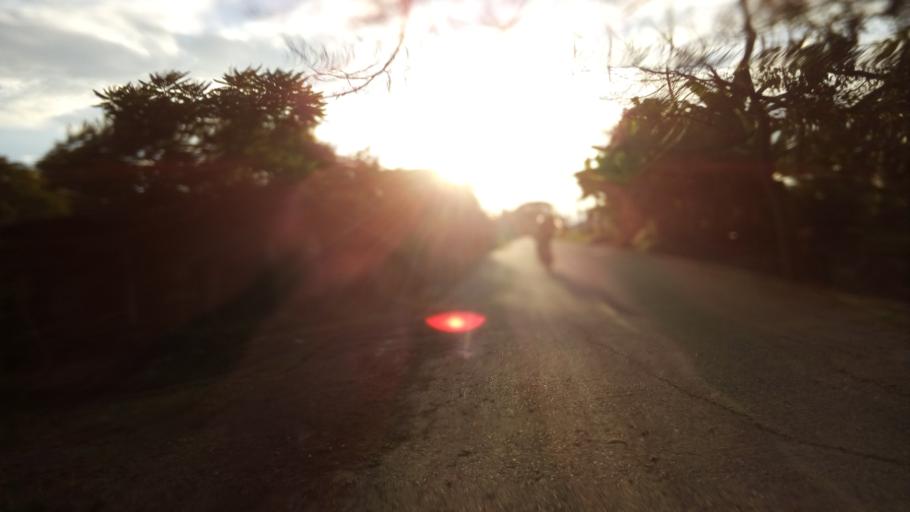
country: TH
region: Pathum Thani
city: Nong Suea
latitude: 14.0754
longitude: 100.8910
